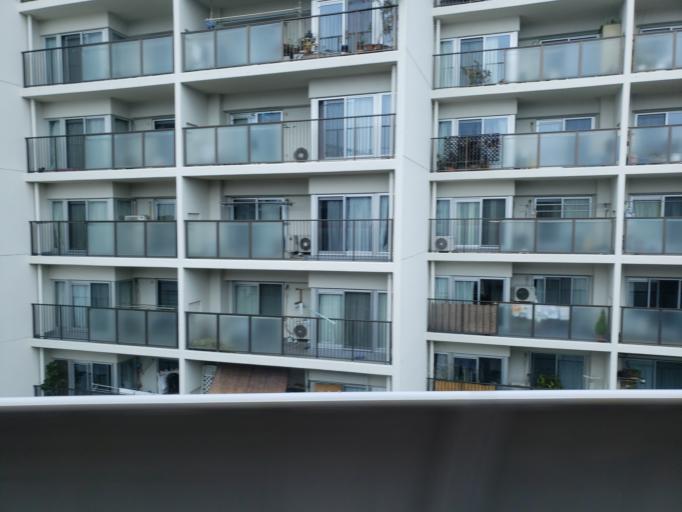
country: JP
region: Hyogo
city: Ashiya
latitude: 34.7154
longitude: 135.2783
